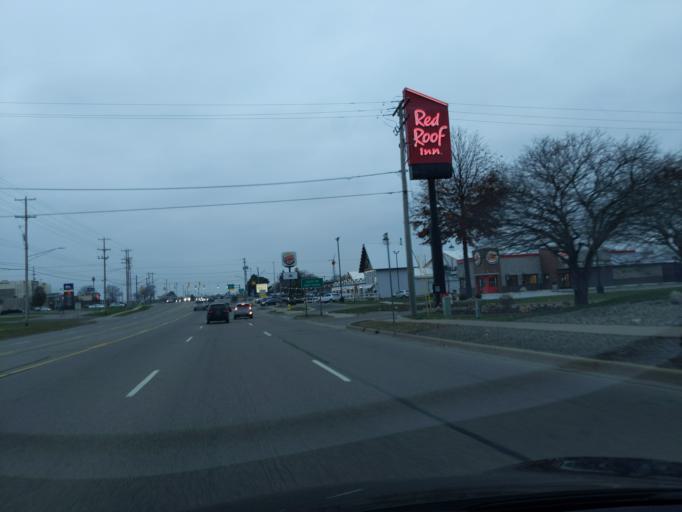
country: US
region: Michigan
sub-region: Eaton County
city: Waverly
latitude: 42.7411
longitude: -84.6593
